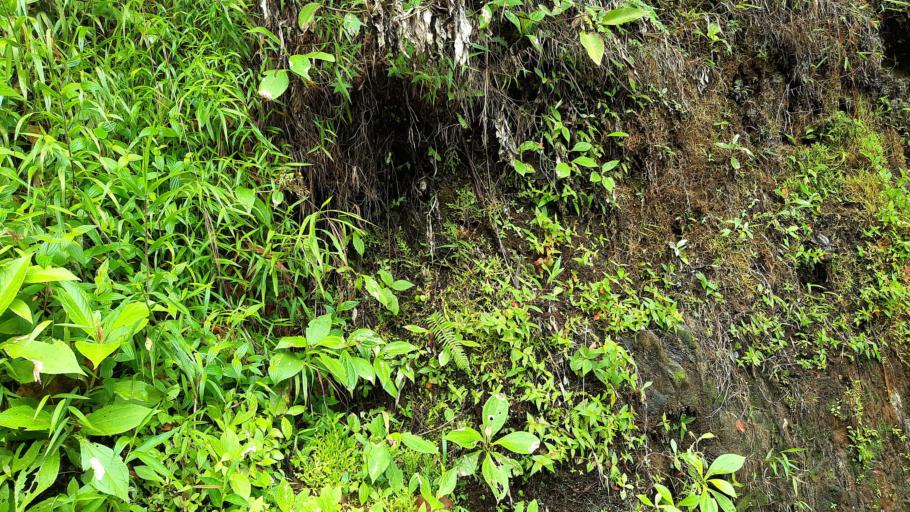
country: CO
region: Boyaca
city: Santa Maria
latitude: 4.9109
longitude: -73.2982
